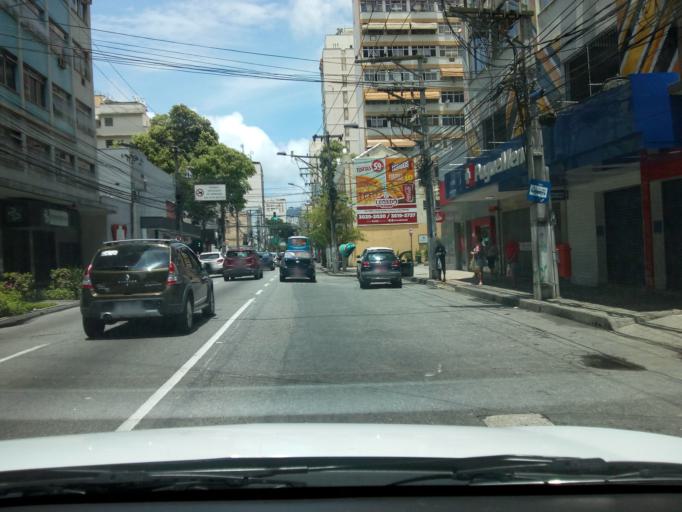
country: BR
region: Rio de Janeiro
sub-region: Niteroi
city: Niteroi
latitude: -22.9023
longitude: -43.1117
